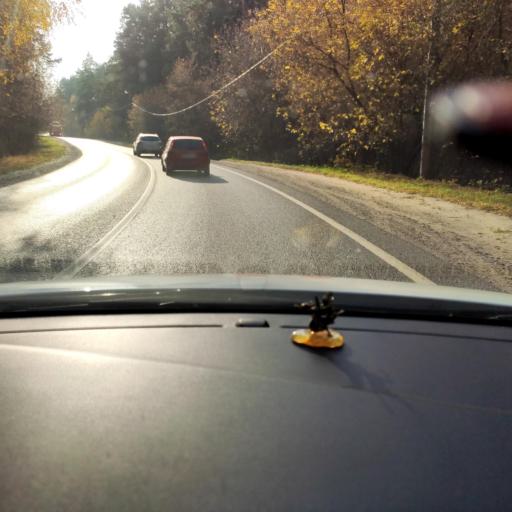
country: RU
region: Tatarstan
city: Osinovo
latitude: 55.8301
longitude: 48.8923
